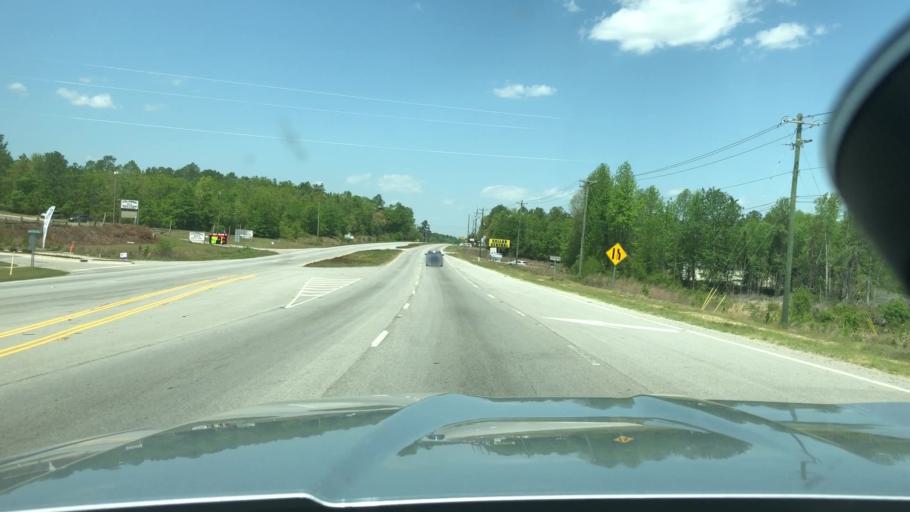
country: US
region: South Carolina
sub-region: Lexington County
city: Pineridge
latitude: 33.8957
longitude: -81.0622
